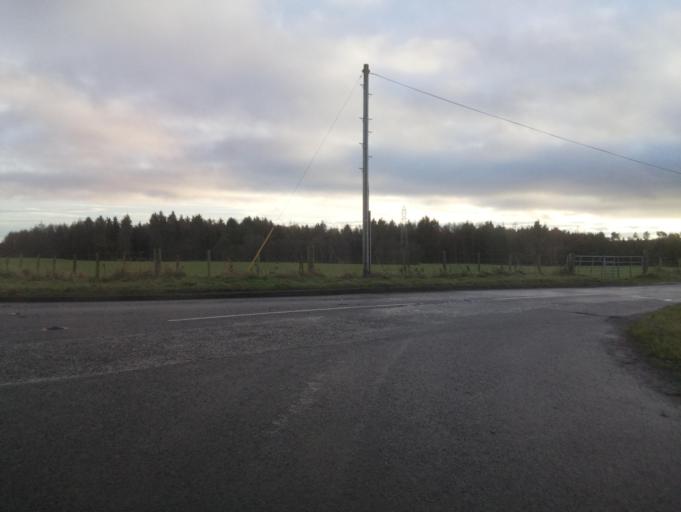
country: GB
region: Scotland
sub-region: Angus
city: Letham
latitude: 56.5533
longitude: -2.7602
